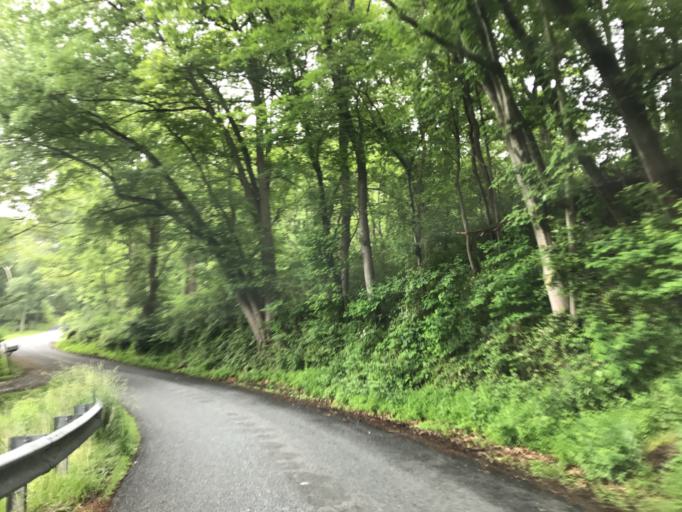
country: US
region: Maryland
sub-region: Harford County
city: Jarrettsville
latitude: 39.7014
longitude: -76.5016
